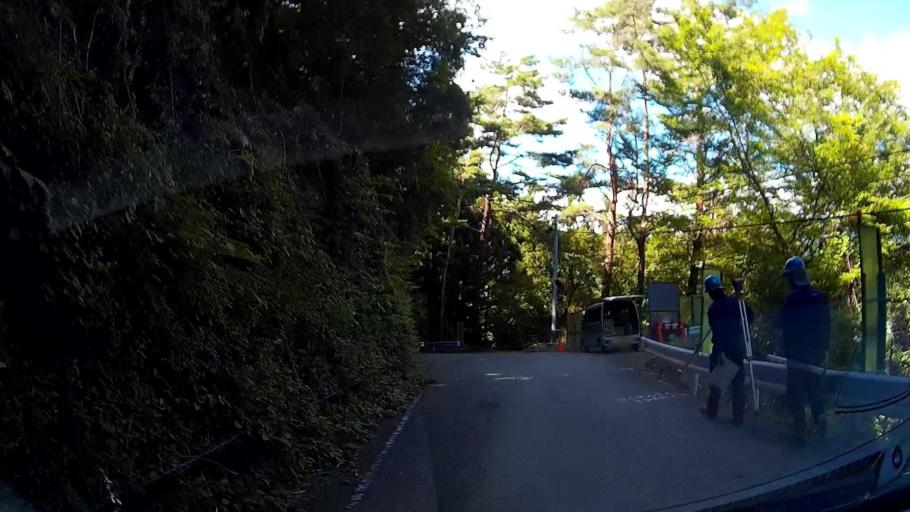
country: JP
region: Shizuoka
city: Shizuoka-shi
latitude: 35.2064
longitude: 138.2351
